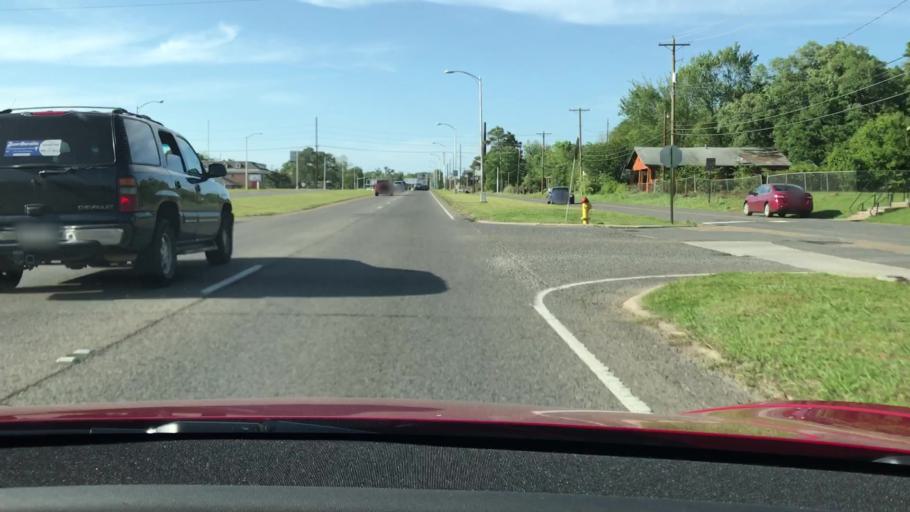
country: US
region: Louisiana
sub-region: Bossier Parish
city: Bossier City
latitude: 32.4963
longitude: -93.7247
